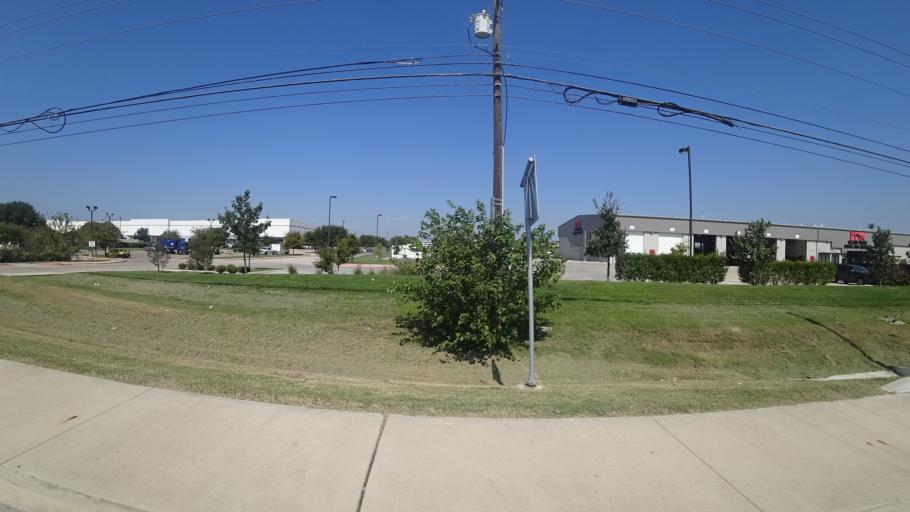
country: US
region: Texas
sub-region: Travis County
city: Manor
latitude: 30.3289
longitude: -97.6569
